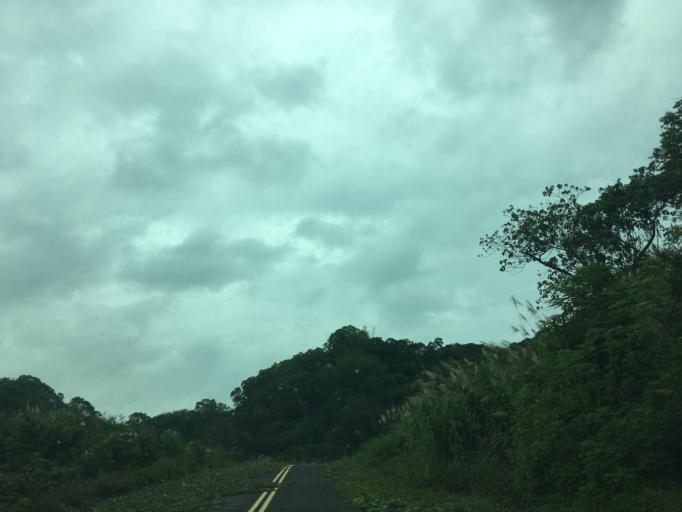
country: TW
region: Taiwan
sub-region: Taichung City
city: Taichung
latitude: 24.0590
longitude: 120.7293
